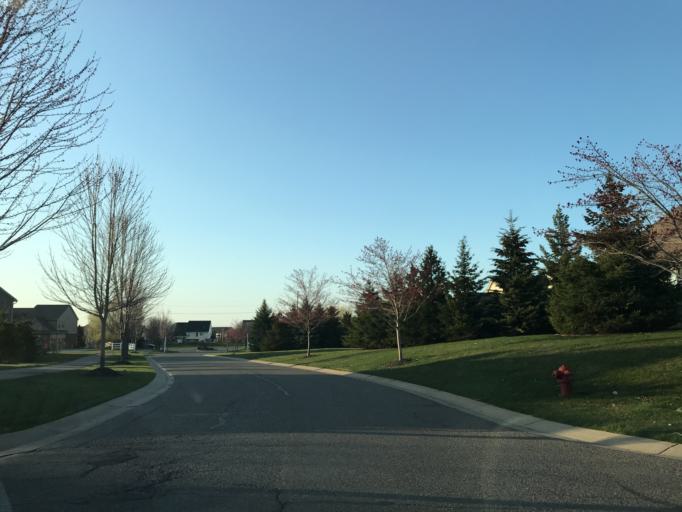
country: US
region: Michigan
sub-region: Oakland County
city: South Lyon
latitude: 42.4611
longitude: -83.5897
